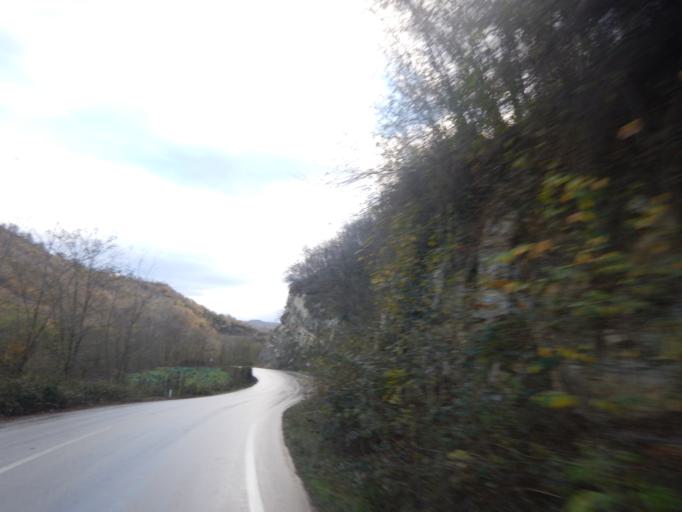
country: TR
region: Ordu
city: Kumru
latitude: 40.9032
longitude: 37.3219
